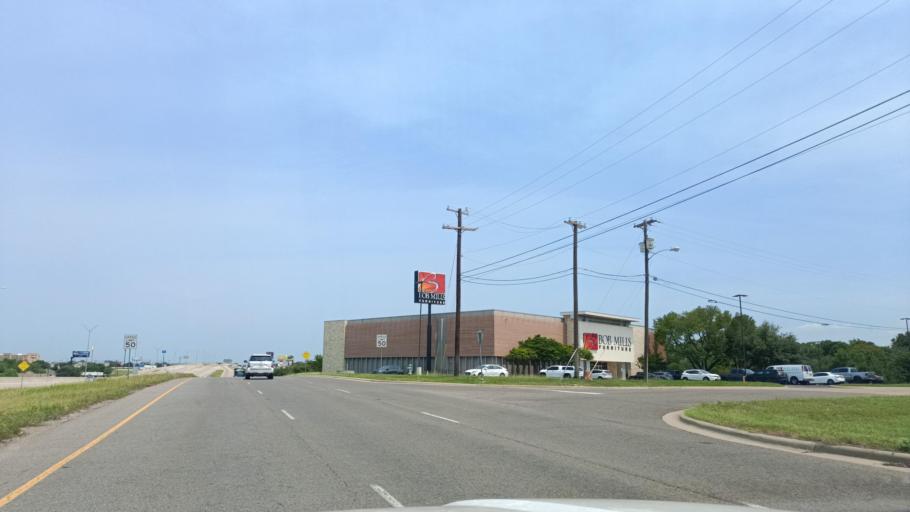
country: US
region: Texas
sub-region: Bell County
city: Temple
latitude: 31.0837
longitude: -97.3837
